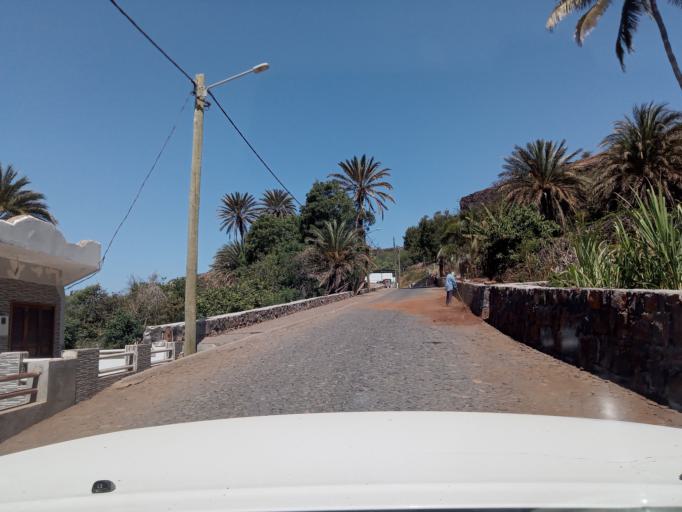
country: CV
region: Ribeira Grande de Santiago
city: Cidade Velha
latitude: 14.9155
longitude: -23.6068
